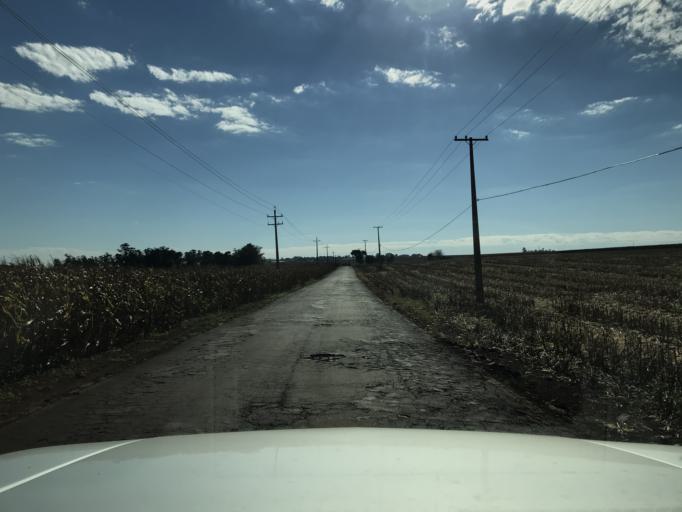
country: BR
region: Parana
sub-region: Palotina
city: Palotina
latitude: -24.2532
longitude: -53.7953
